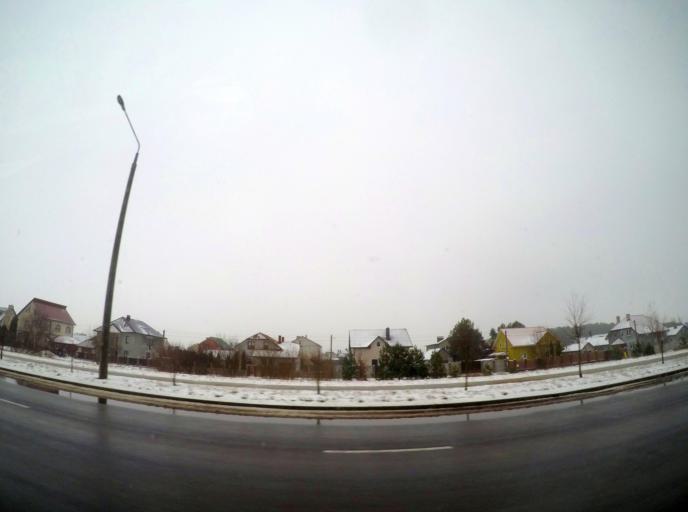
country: BY
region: Grodnenskaya
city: Hrodna
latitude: 53.6188
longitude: 23.8219
